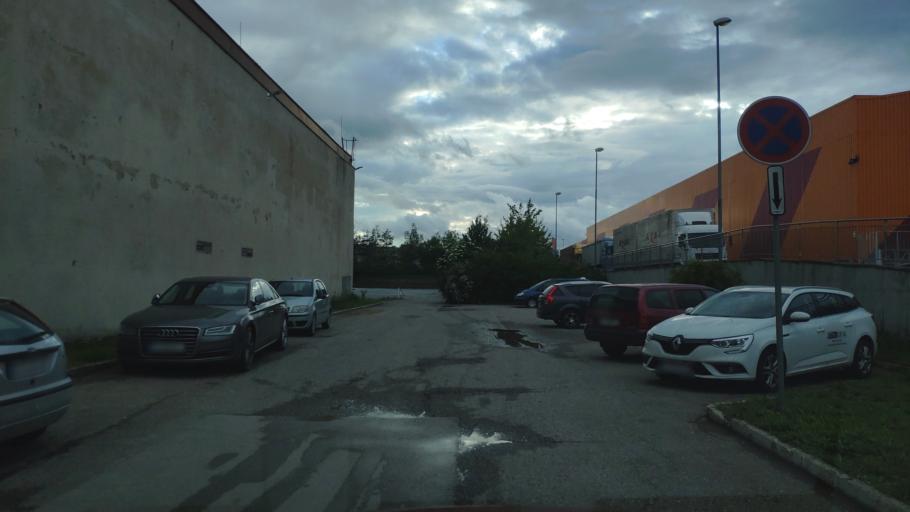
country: SK
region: Kosicky
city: Kosice
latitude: 48.6993
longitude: 21.2427
